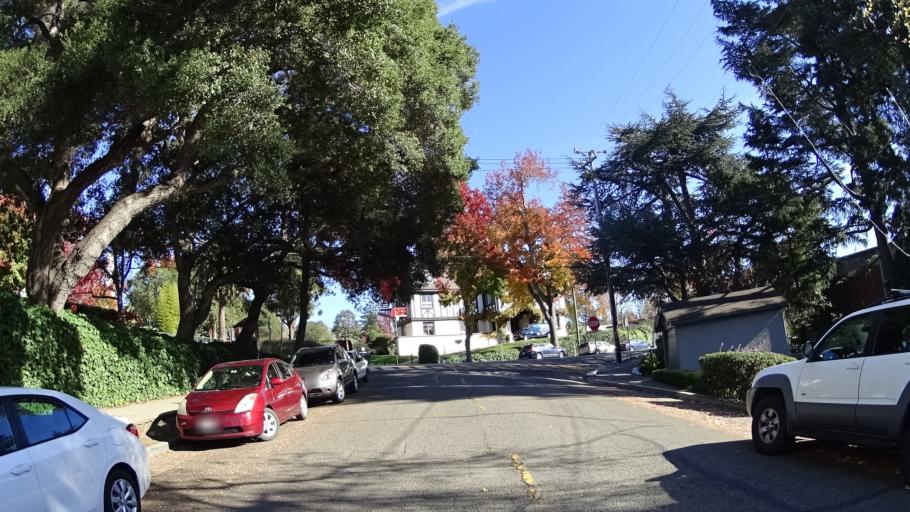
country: US
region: California
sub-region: Alameda County
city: Piedmont
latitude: 37.8231
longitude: -122.2349
